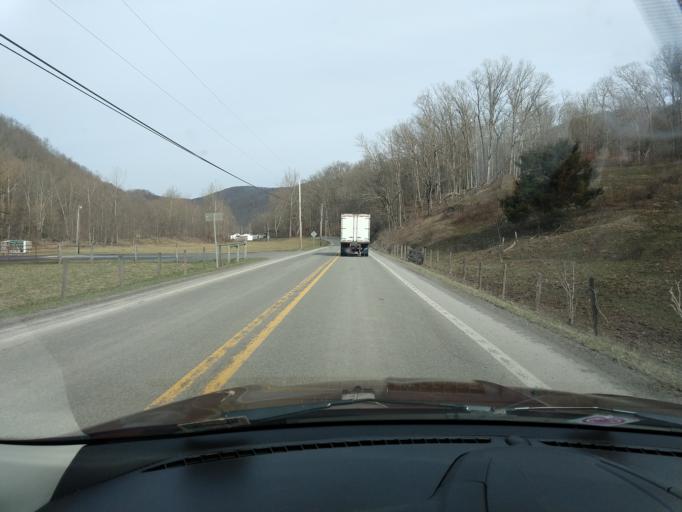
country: US
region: West Virginia
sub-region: Pendleton County
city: Franklin
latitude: 38.8499
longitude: -79.4233
